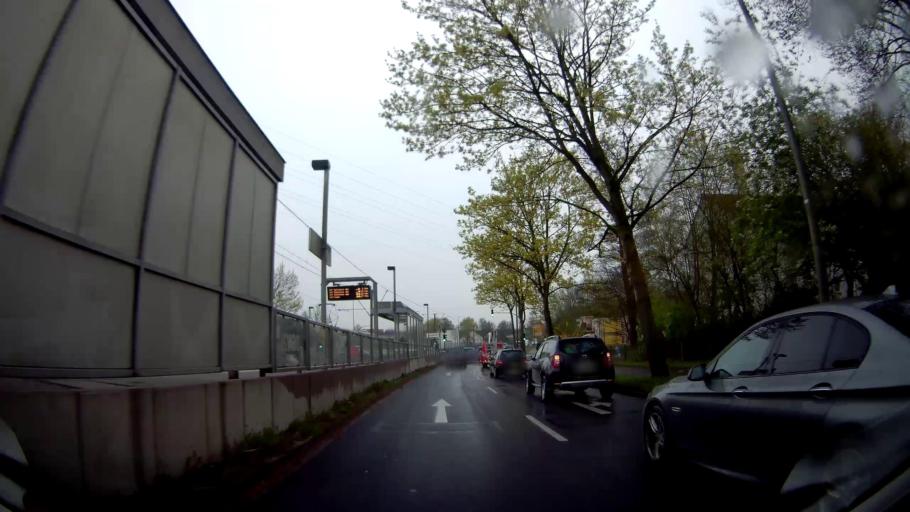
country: DE
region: North Rhine-Westphalia
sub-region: Regierungsbezirk Arnsberg
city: Dortmund
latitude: 51.5261
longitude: 7.4236
